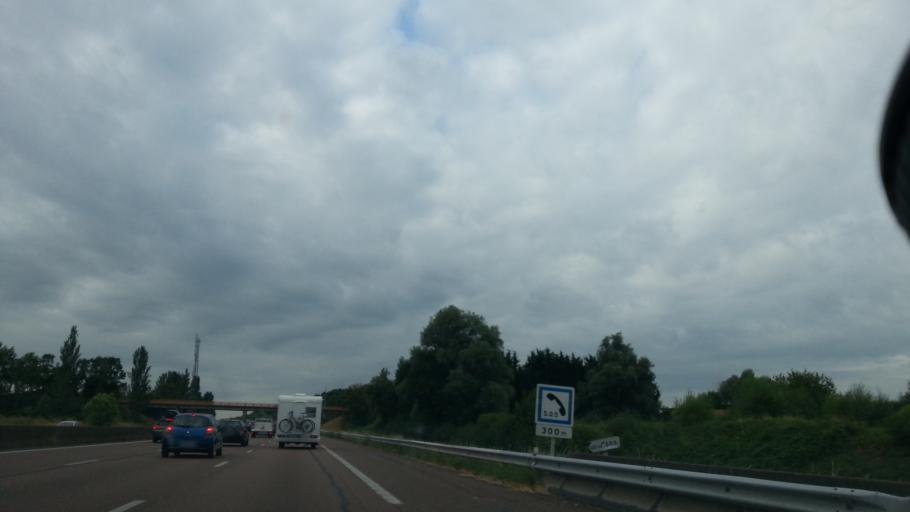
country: FR
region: Bourgogne
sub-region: Departement de Saone-et-Loire
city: Demigny
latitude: 46.9241
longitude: 4.8191
